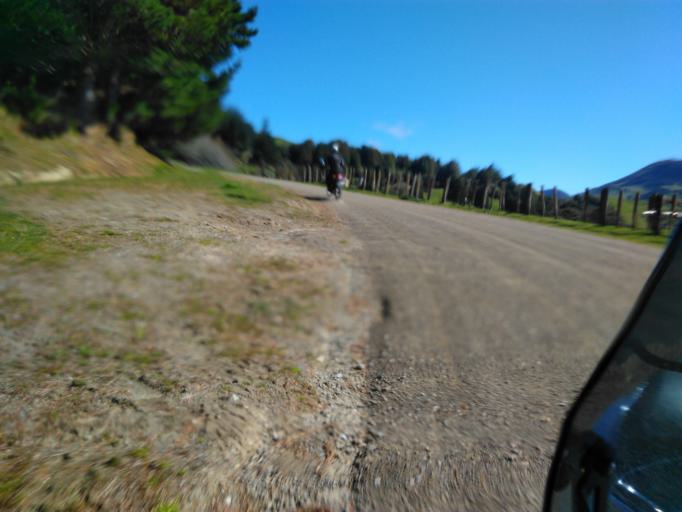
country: NZ
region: Bay of Plenty
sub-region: Opotiki District
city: Opotiki
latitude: -38.3653
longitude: 177.5982
